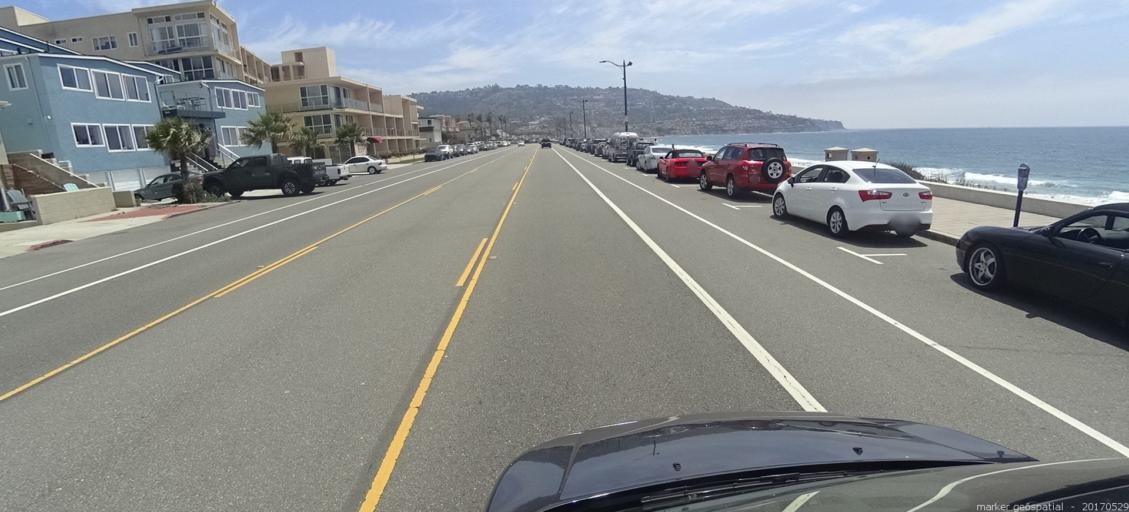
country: US
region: California
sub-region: Los Angeles County
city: Palos Verdes Estates
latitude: 33.8182
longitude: -118.3901
